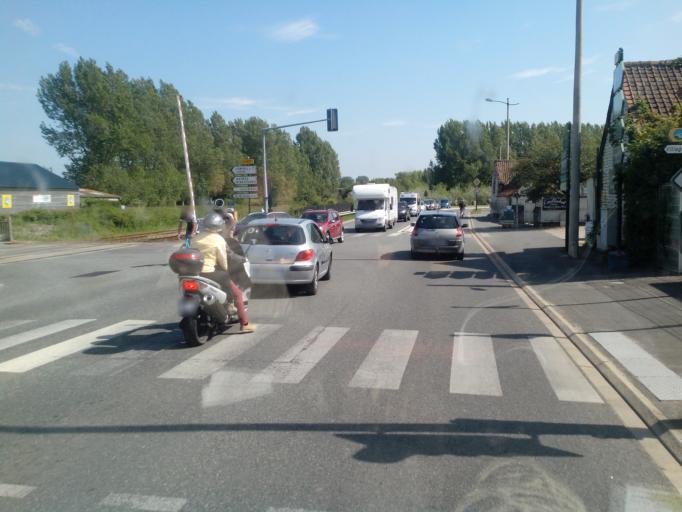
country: FR
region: Nord-Pas-de-Calais
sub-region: Departement du Pas-de-Calais
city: Verton
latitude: 50.3732
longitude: 1.6602
